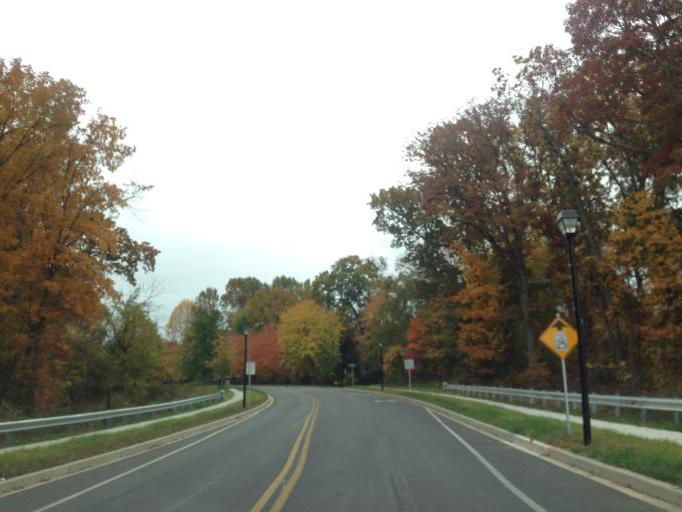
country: US
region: Maryland
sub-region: Howard County
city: Columbia
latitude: 39.3015
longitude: -76.8778
